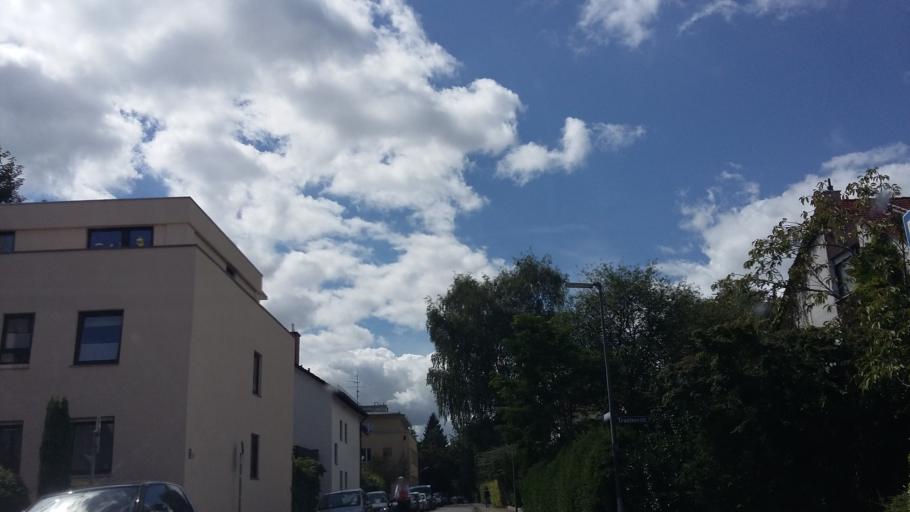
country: DE
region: Bavaria
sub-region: Upper Bavaria
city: Pasing
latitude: 48.1454
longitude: 11.4512
